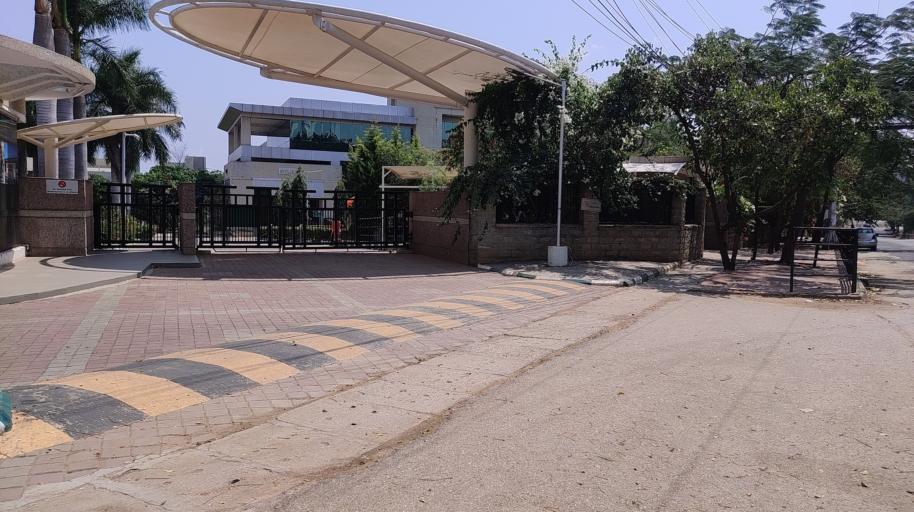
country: IN
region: Karnataka
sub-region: Bangalore Rural
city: Hoskote
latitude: 12.9747
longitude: 77.7271
